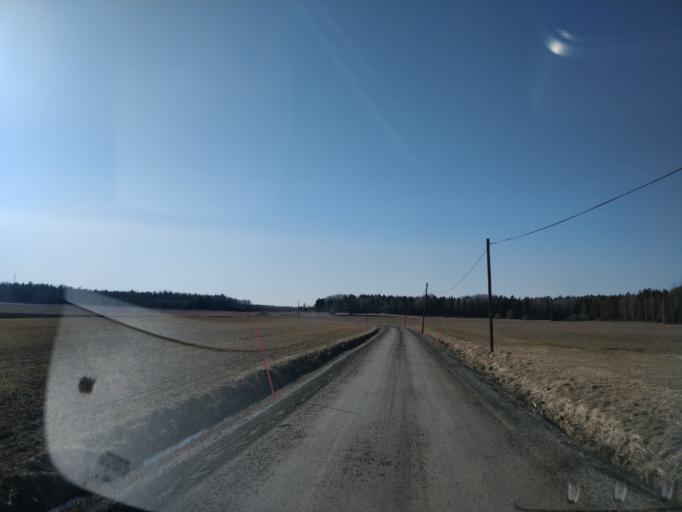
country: SE
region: Uppsala
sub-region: Enkopings Kommun
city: Orsundsbro
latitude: 59.8252
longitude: 17.1338
